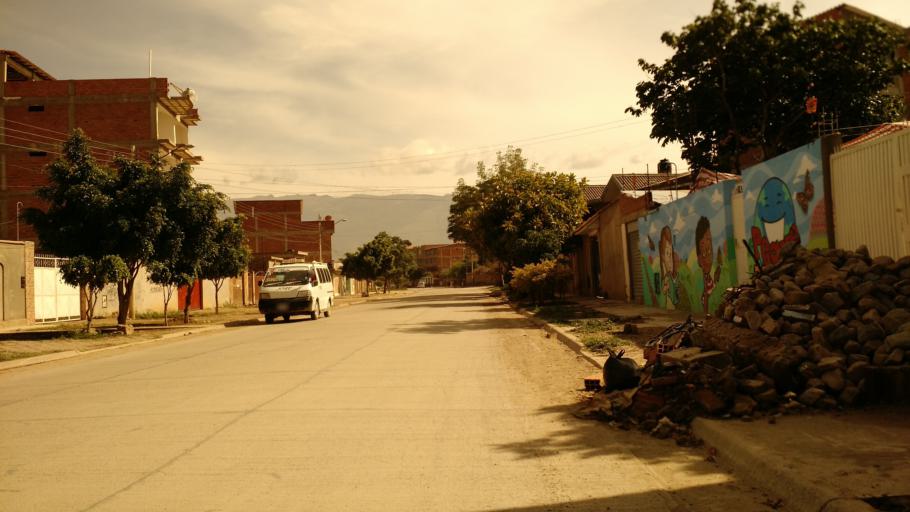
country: BO
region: Cochabamba
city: Cochabamba
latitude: -17.4324
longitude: -66.1594
